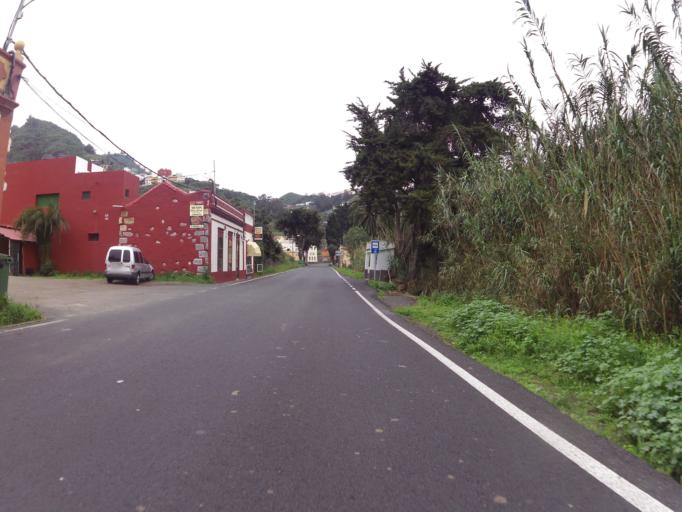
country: ES
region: Canary Islands
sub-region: Provincia de Las Palmas
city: Teror
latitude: 28.0697
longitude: -15.5255
